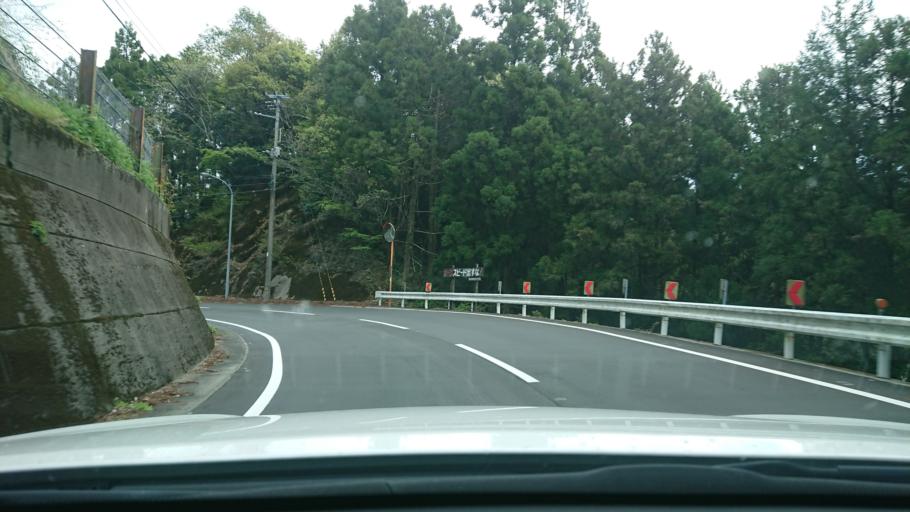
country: JP
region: Tokushima
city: Ishii
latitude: 33.9057
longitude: 134.4206
